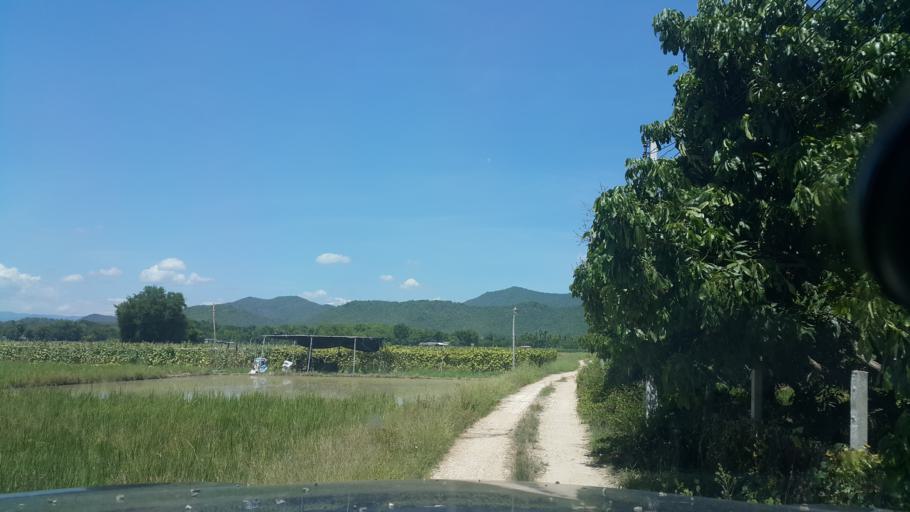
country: TH
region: Chiang Mai
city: San Kamphaeng
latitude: 18.7004
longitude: 99.1515
